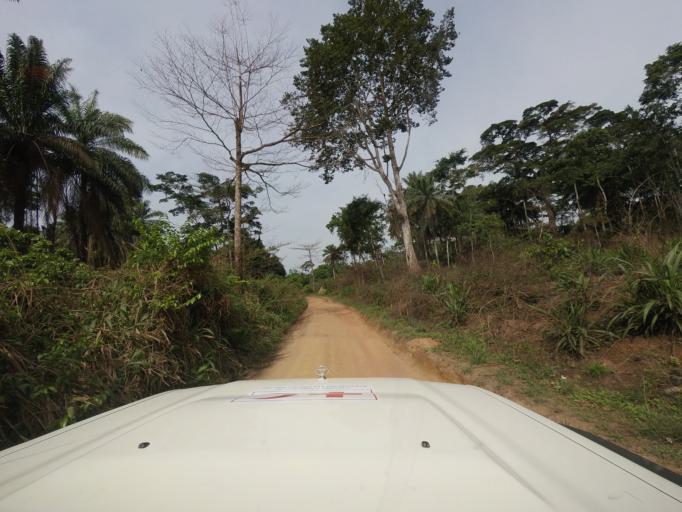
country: GN
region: Nzerekore
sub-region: Macenta
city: Macenta
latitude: 8.4747
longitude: -9.5657
